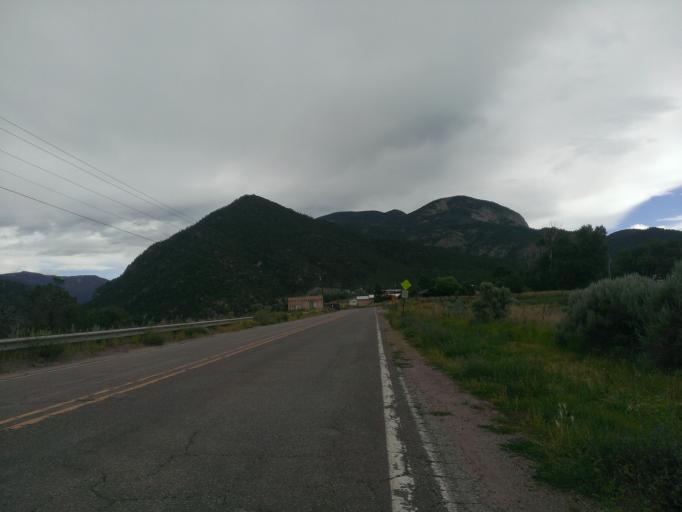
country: US
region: New Mexico
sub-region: Taos County
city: Arroyo Seco
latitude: 36.5326
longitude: -105.5689
